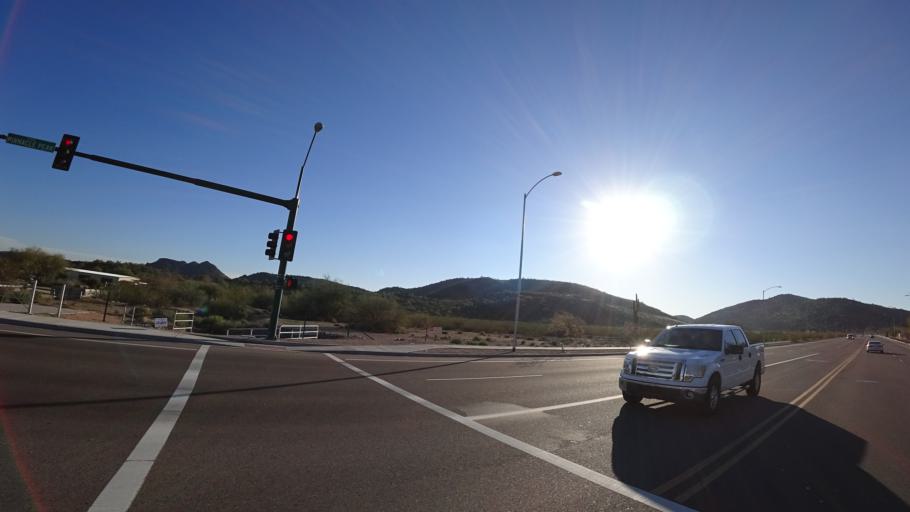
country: US
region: Arizona
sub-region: Maricopa County
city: Peoria
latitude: 33.6980
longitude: -112.1697
